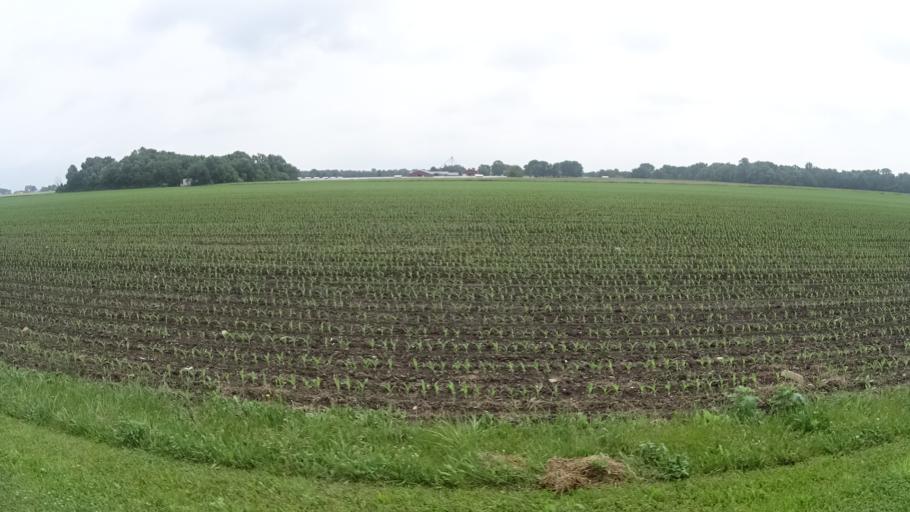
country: US
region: Ohio
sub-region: Huron County
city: Bellevue
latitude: 41.3515
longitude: -82.7944
